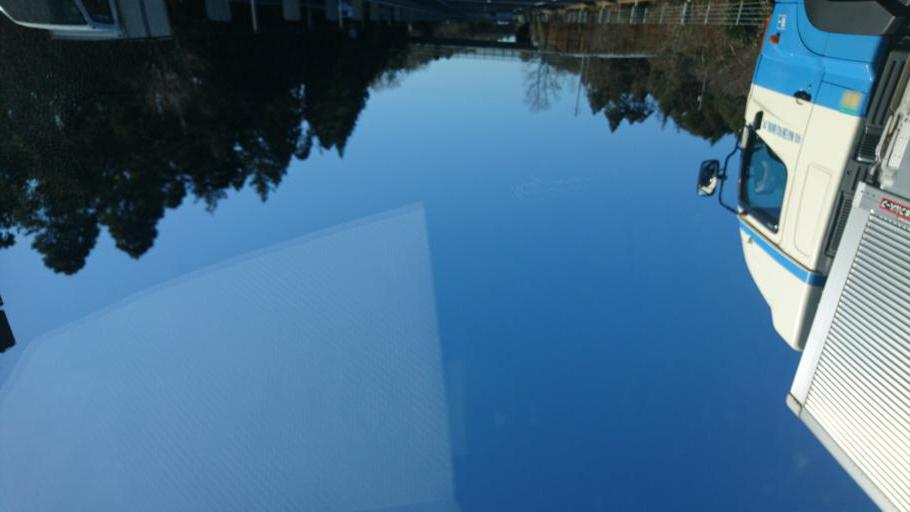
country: JP
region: Chiba
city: Oami
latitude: 35.5689
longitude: 140.2516
